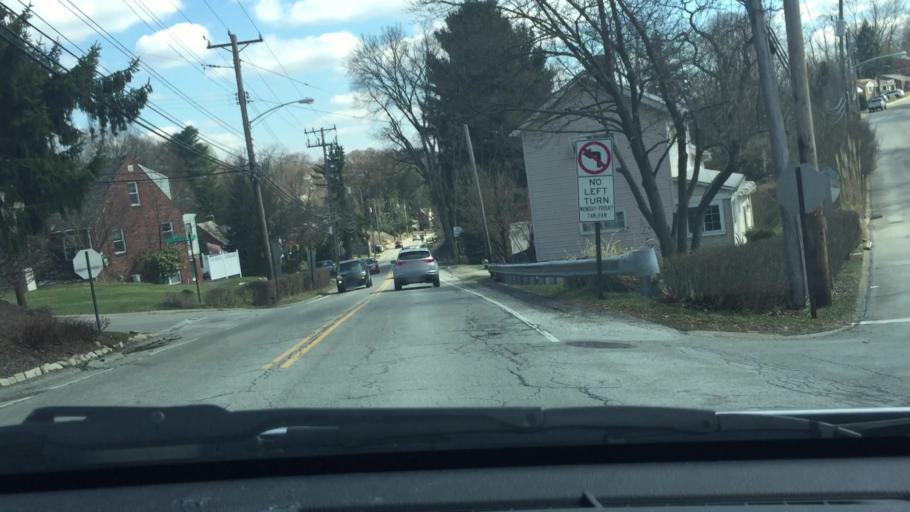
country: US
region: Pennsylvania
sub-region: Allegheny County
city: Green Tree
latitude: 40.4081
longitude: -80.0489
